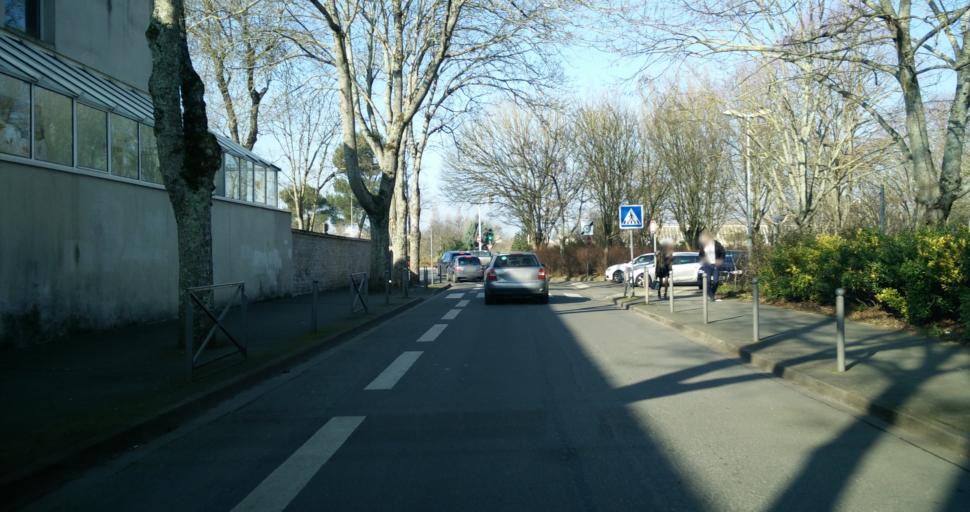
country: FR
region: Poitou-Charentes
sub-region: Departement de la Charente-Maritime
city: La Rochelle
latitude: 46.1664
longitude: -1.1523
